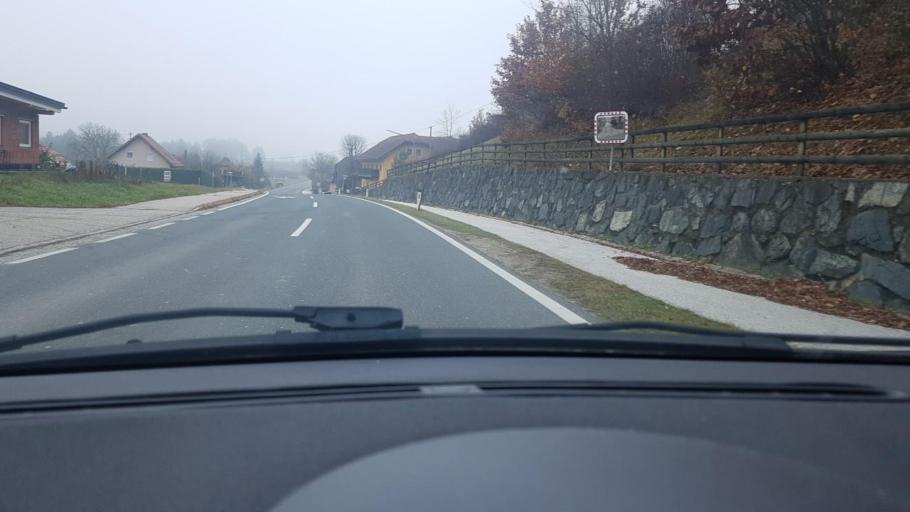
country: AT
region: Carinthia
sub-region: Politischer Bezirk Volkermarkt
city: Bleiburg/Pliberk
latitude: 46.6122
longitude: 14.8007
